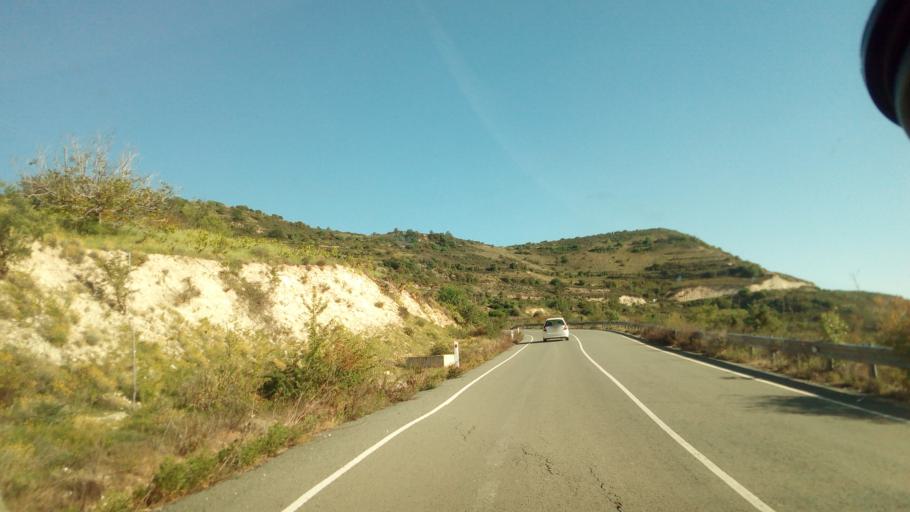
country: CY
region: Limassol
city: Pachna
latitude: 34.8624
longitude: 32.7599
